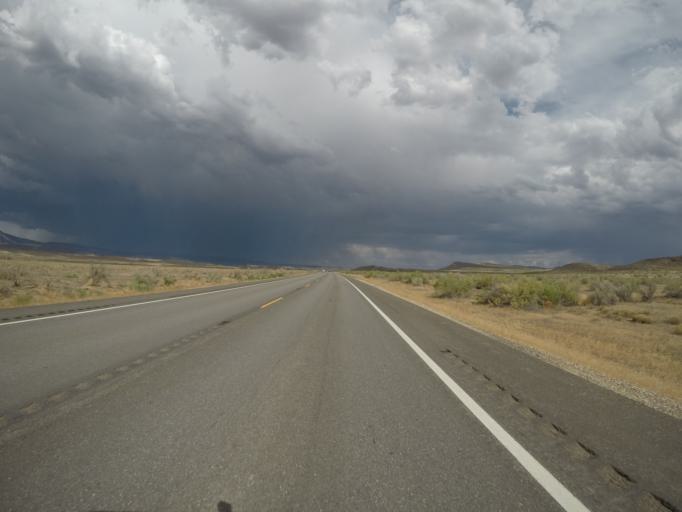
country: US
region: Utah
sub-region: Uintah County
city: Naples
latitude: 40.2921
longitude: -109.1708
